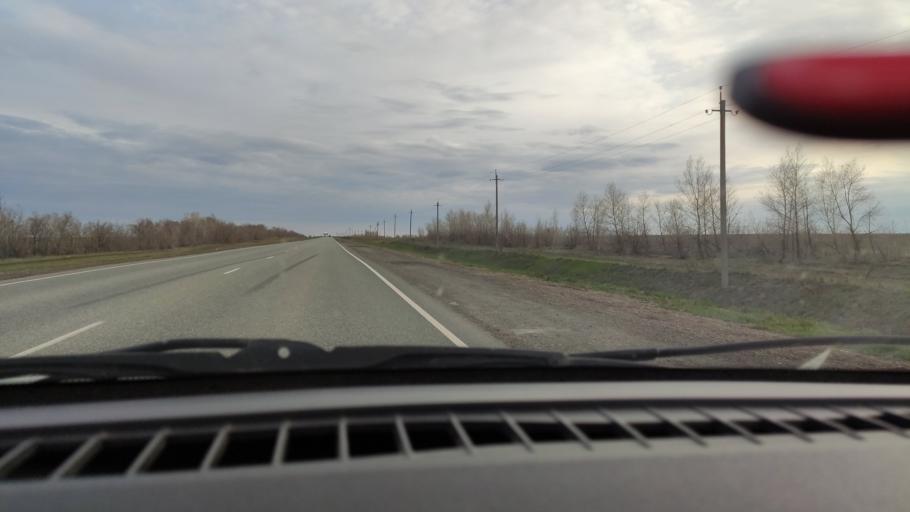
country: RU
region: Orenburg
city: Tatarskaya Kargala
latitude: 52.0096
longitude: 55.2030
